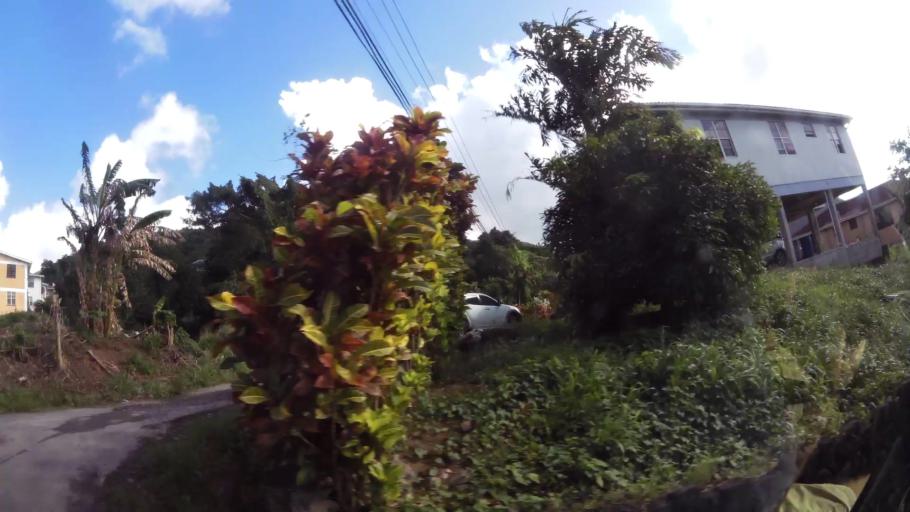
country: DM
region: Saint George
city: Roseau
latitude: 15.2852
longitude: -61.3681
